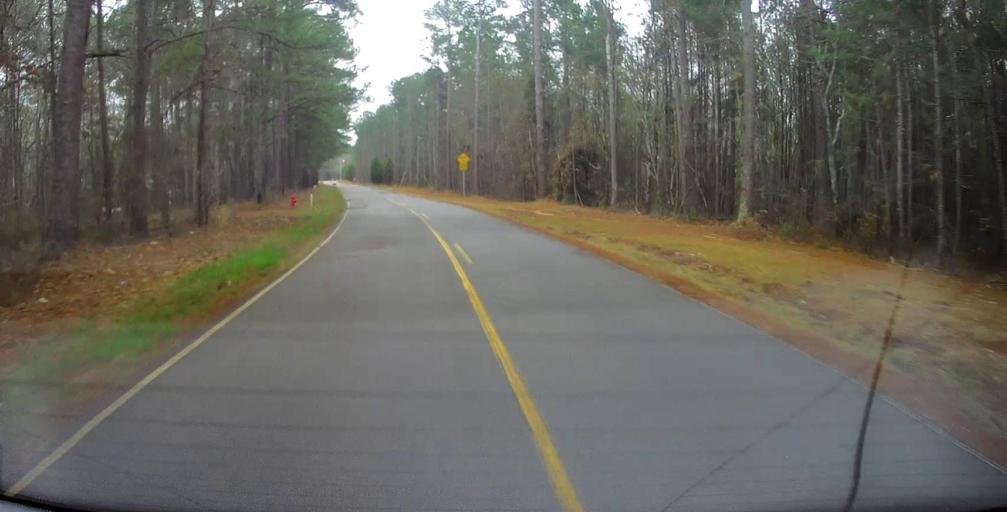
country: US
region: Georgia
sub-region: Monroe County
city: Forsyth
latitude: 33.0203
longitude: -83.8572
